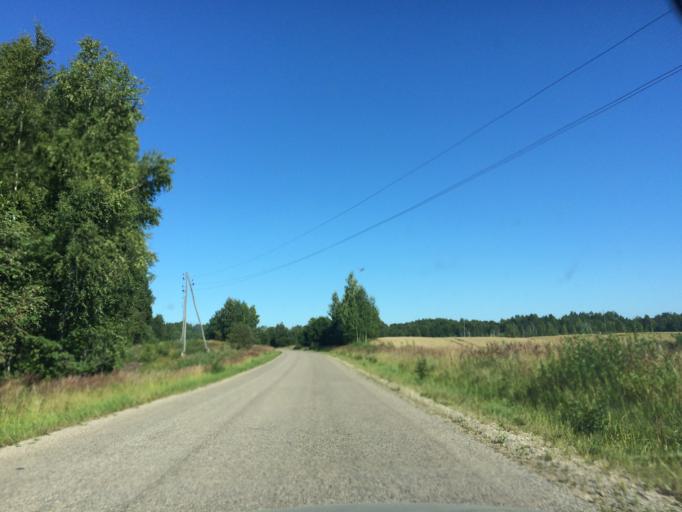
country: LV
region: Rezekne
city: Rezekne
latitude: 56.4885
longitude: 27.2541
